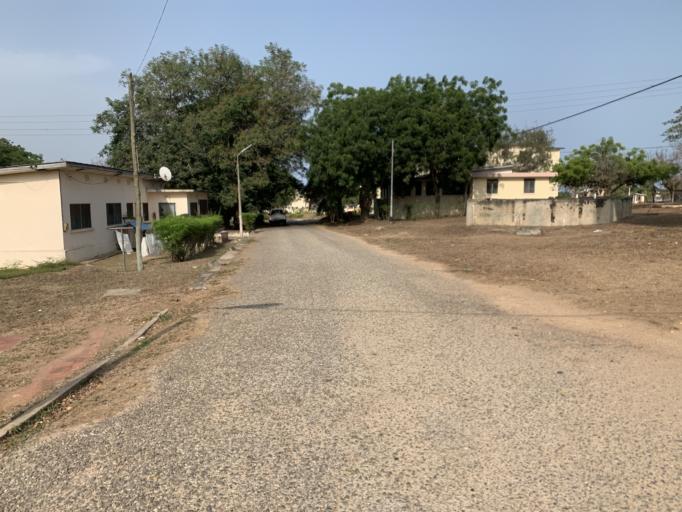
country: GH
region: Central
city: Winneba
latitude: 5.3377
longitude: -0.6271
